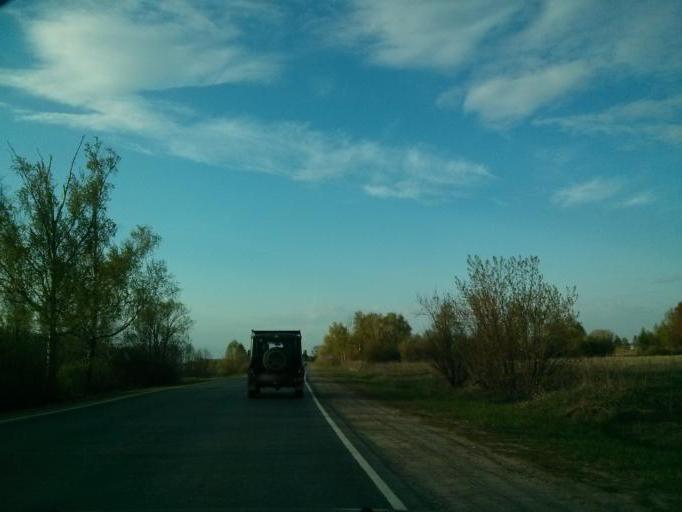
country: RU
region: Nizjnij Novgorod
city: Navashino
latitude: 55.6220
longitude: 42.2303
